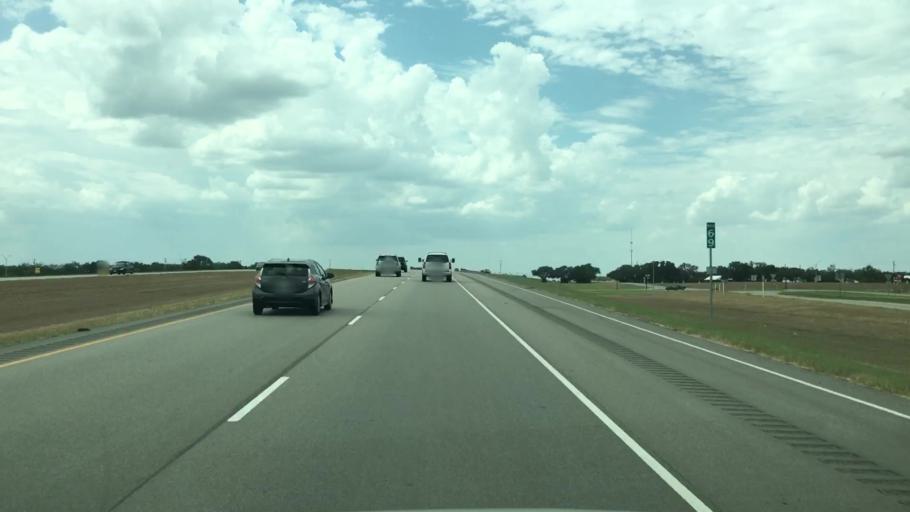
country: US
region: Texas
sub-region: Live Oak County
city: Three Rivers
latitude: 28.4873
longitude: -98.1400
